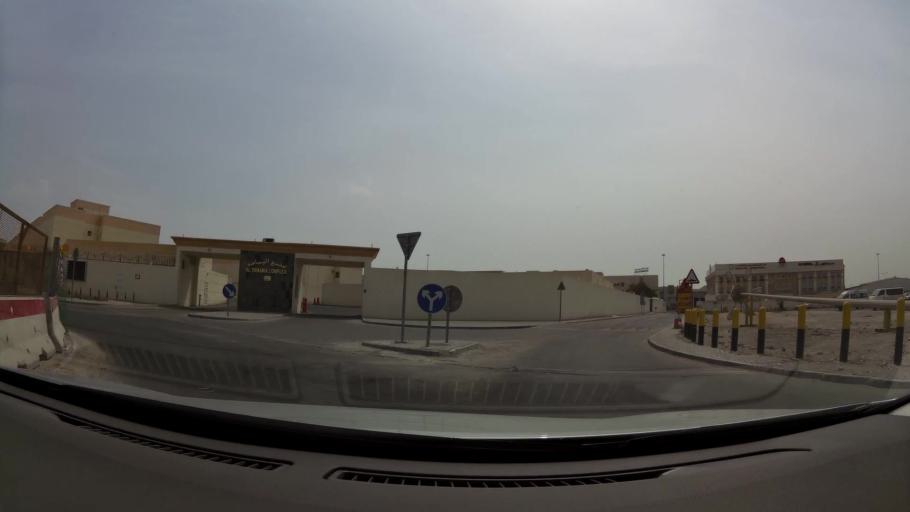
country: QA
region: Baladiyat ad Dawhah
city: Doha
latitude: 25.2612
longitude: 51.4846
